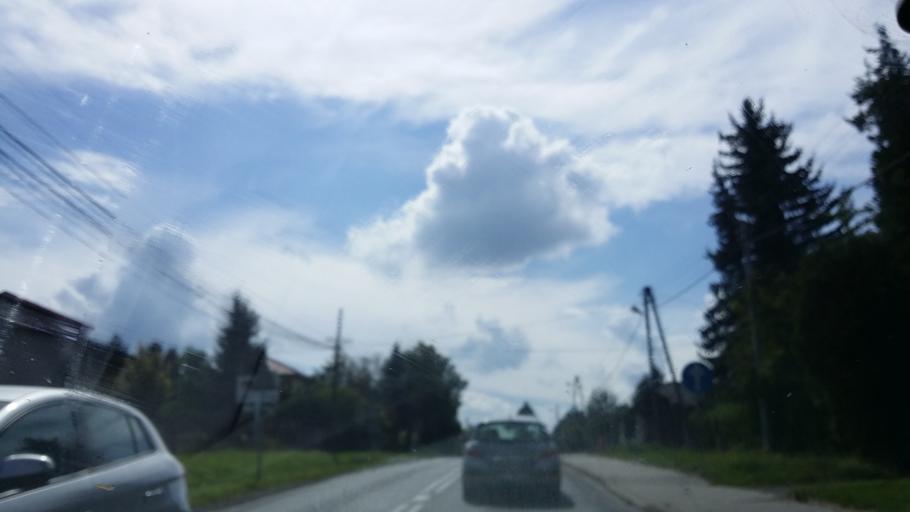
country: PL
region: Lesser Poland Voivodeship
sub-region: Powiat wielicki
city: Wieliczka
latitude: 49.9893
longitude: 20.0797
